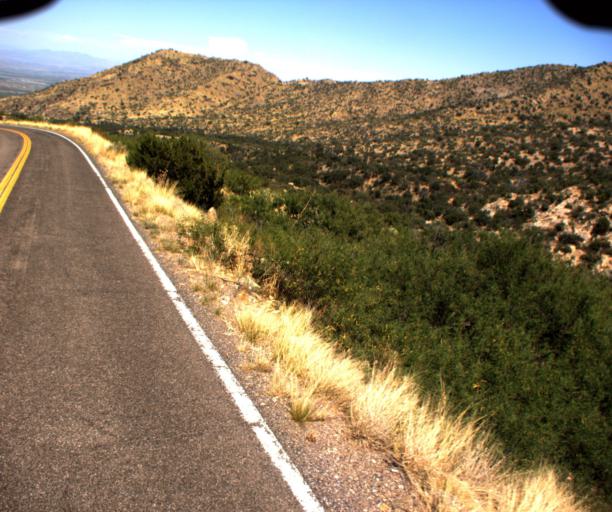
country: US
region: Arizona
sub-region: Graham County
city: Swift Trail Junction
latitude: 32.6702
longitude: -109.7868
